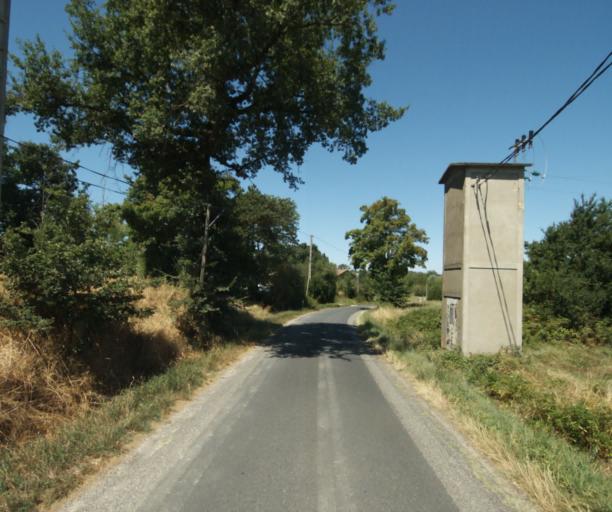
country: FR
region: Midi-Pyrenees
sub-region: Departement de la Haute-Garonne
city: Saint-Felix-Lauragais
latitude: 43.4788
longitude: 1.9272
